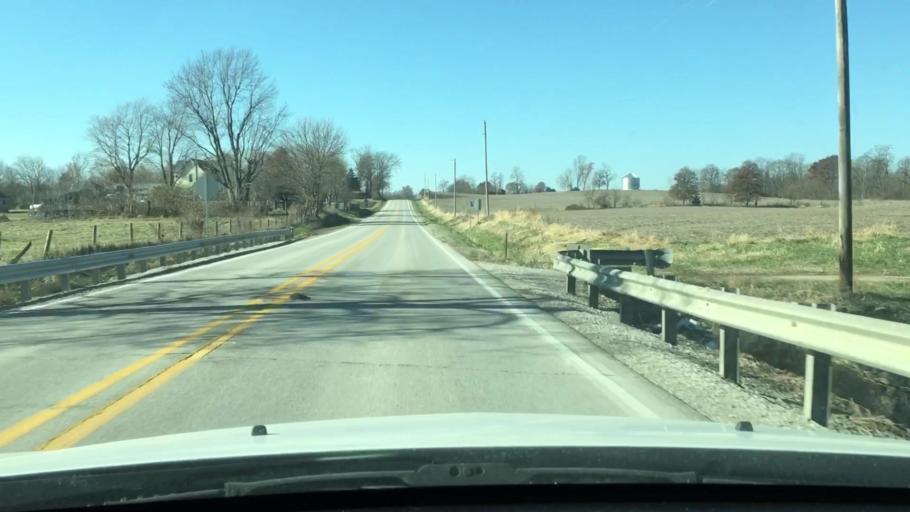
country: US
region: Illinois
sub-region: Pike County
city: Pittsfield
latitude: 39.6139
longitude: -90.7399
